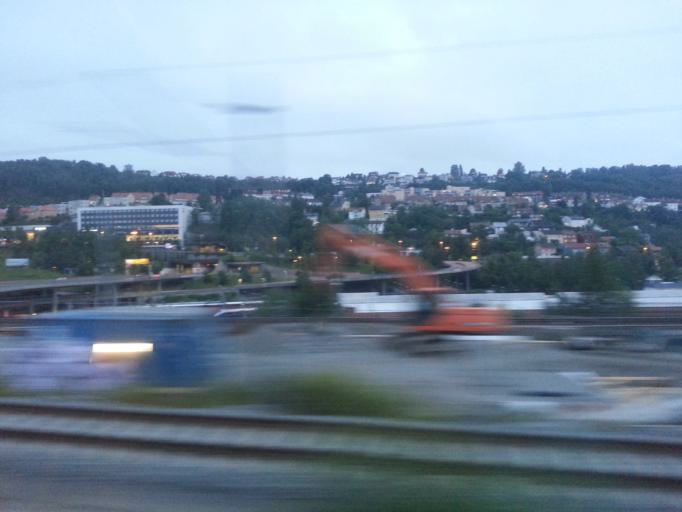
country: NO
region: Oslo
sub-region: Oslo
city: Oslo
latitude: 59.9059
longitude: 10.7831
